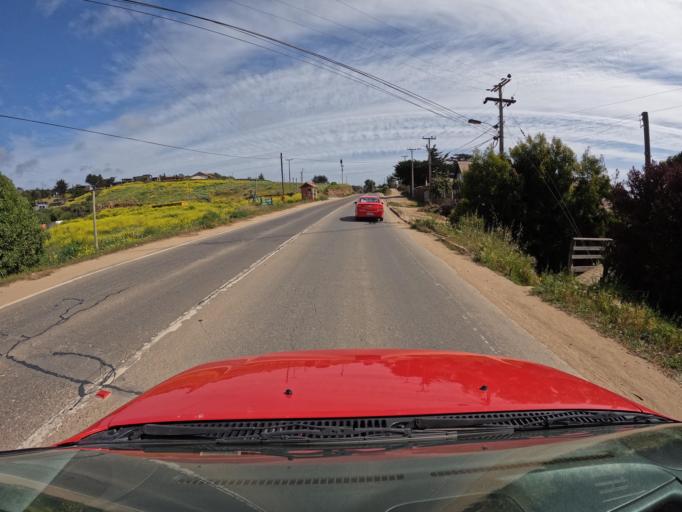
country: CL
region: O'Higgins
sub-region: Provincia de Colchagua
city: Santa Cruz
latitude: -34.4151
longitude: -72.0287
